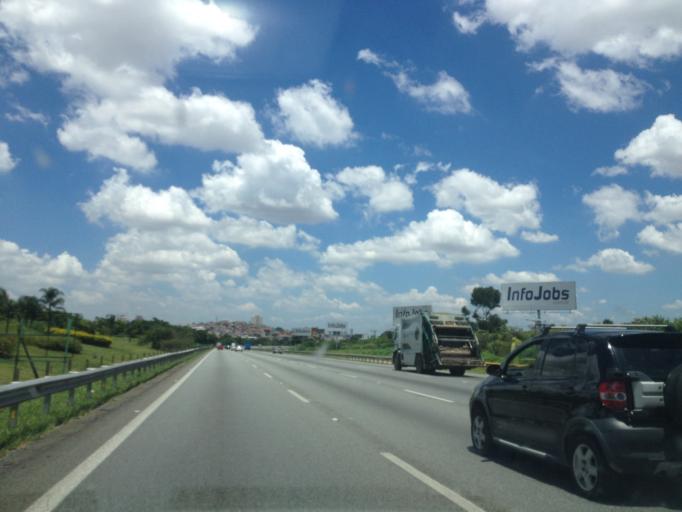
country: BR
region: Sao Paulo
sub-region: Guarulhos
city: Guarulhos
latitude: -23.4984
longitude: -46.5438
